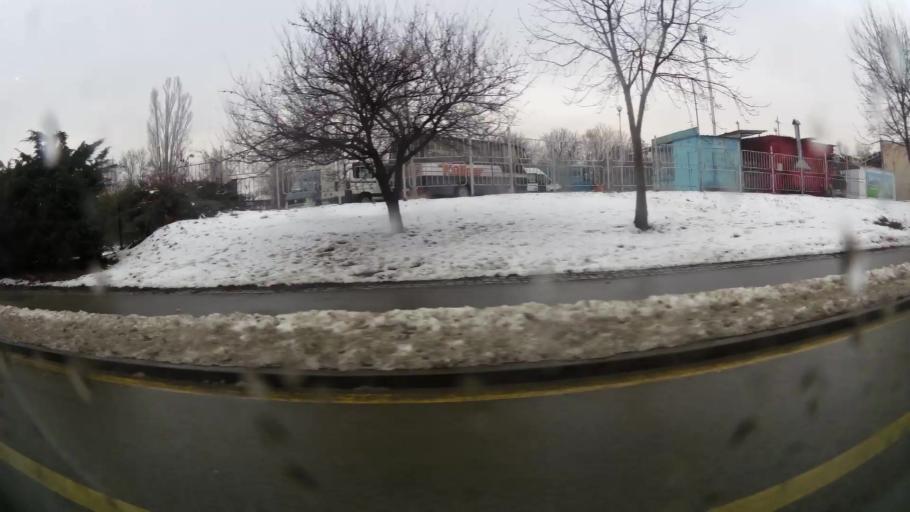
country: BG
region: Sofia-Capital
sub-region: Stolichna Obshtina
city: Sofia
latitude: 42.6730
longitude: 23.2710
